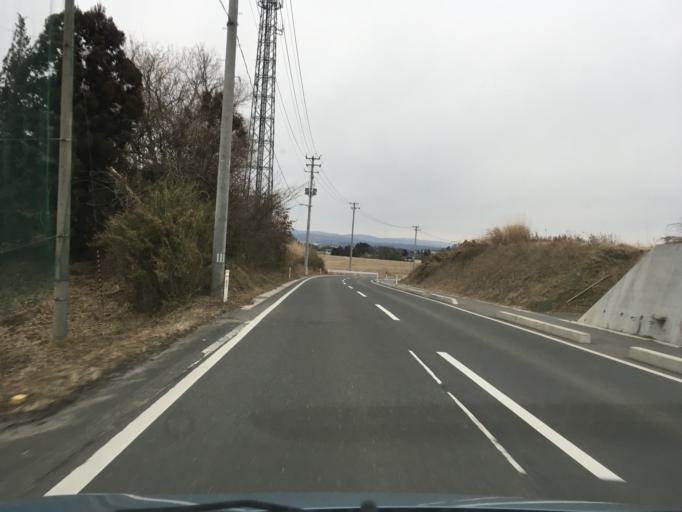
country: JP
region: Miyagi
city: Wakuya
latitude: 38.6962
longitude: 141.1702
